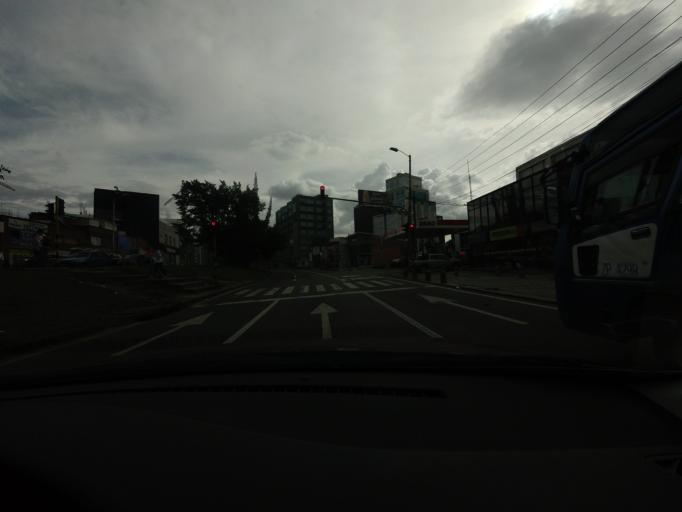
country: CO
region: Bogota D.C.
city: Barrio San Luis
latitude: 4.6981
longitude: -74.0305
